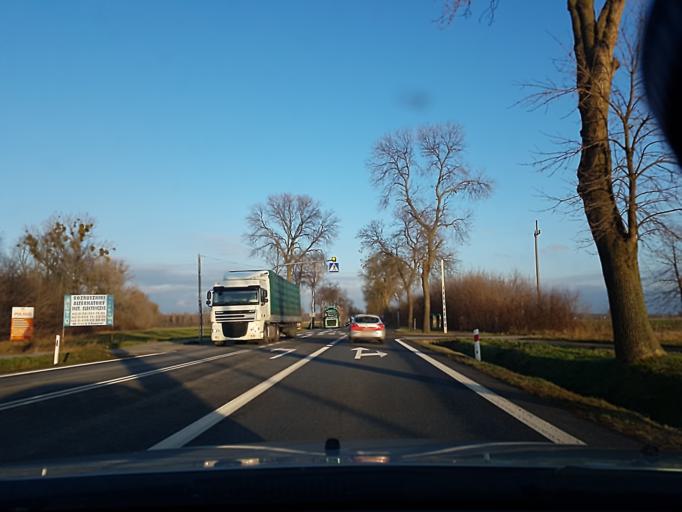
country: PL
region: Masovian Voivodeship
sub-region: Powiat plocki
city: Lack
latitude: 52.4585
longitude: 19.5863
